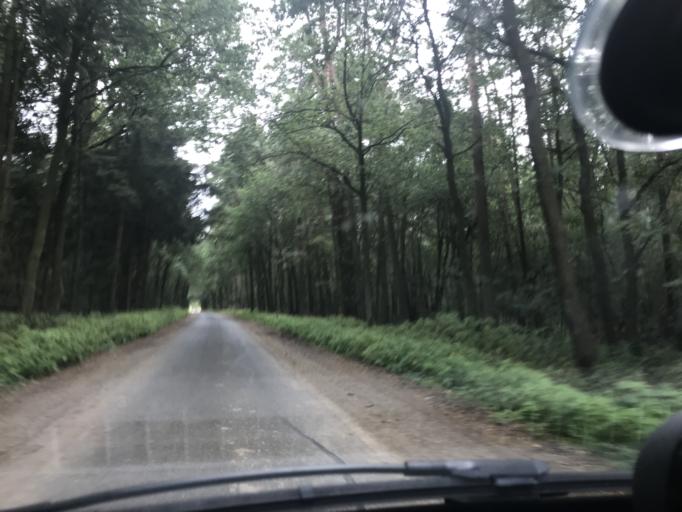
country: DE
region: Lower Saxony
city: Moisburg
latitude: 53.3941
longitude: 9.7245
